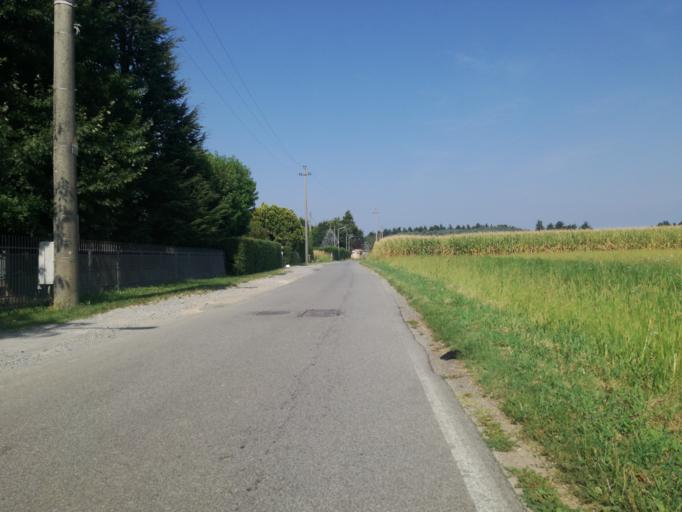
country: IT
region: Lombardy
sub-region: Provincia di Monza e Brianza
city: Cornate d'Adda
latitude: 45.6268
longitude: 9.4830
